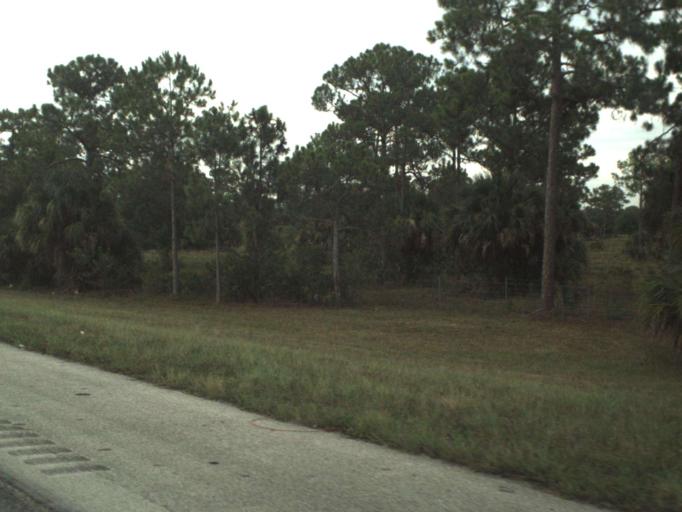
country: US
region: Florida
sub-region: Martin County
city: Palm City
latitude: 27.1267
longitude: -80.3214
